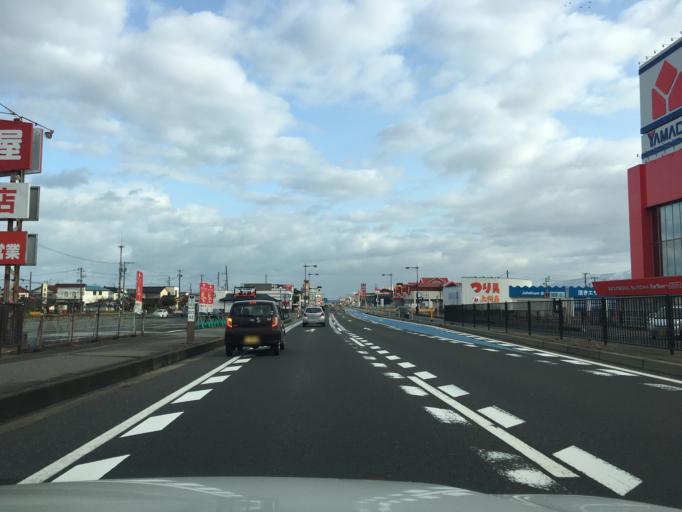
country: JP
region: Yamagata
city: Sakata
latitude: 38.9149
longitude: 139.8581
